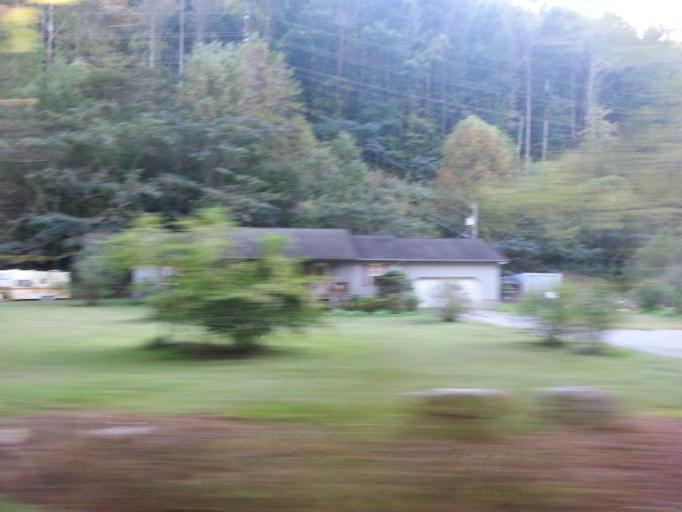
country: US
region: Tennessee
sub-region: Sevier County
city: Pigeon Forge
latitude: 35.6906
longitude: -83.6986
